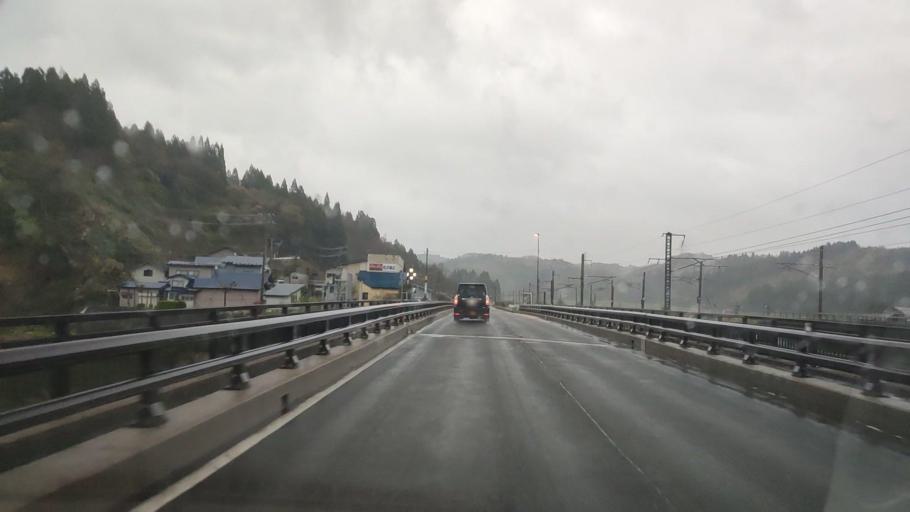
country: JP
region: Akita
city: Akita
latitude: 39.6549
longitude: 140.2464
